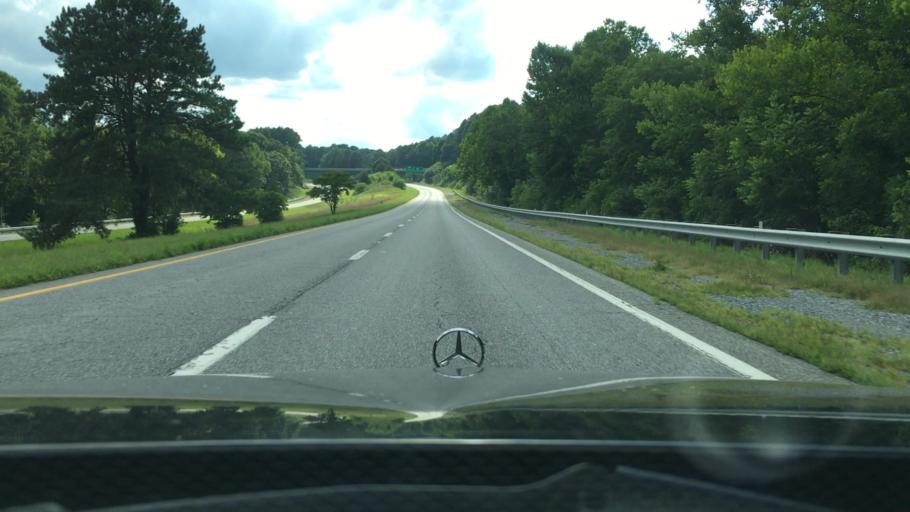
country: US
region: Virginia
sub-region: Campbell County
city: Altavista
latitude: 37.1369
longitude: -79.2841
